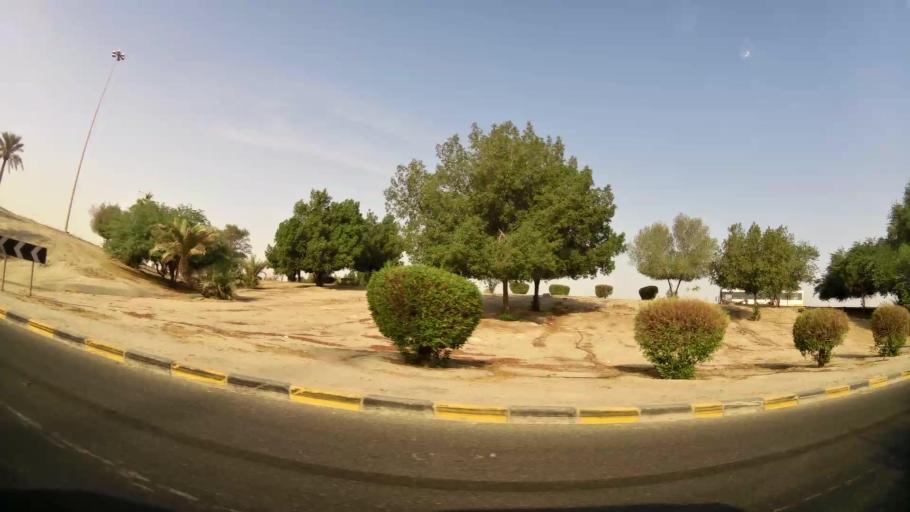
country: KW
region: Al Farwaniyah
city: Janub as Surrah
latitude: 29.2664
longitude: 47.9855
